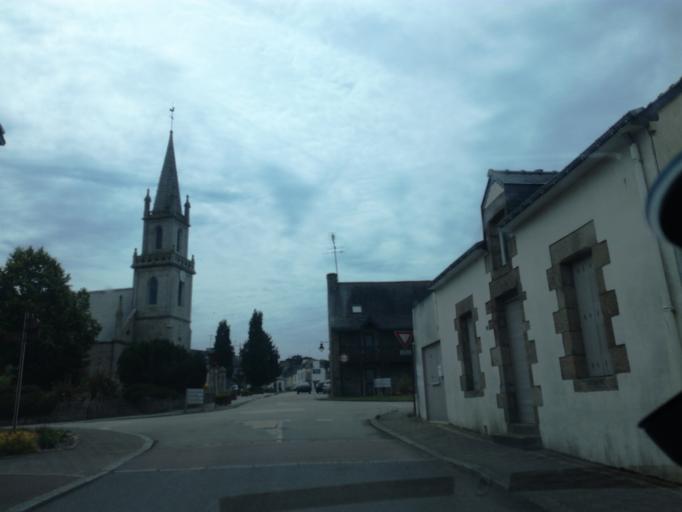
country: FR
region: Brittany
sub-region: Departement du Morbihan
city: Saint-Thuriau
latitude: 48.0169
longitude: -2.9506
